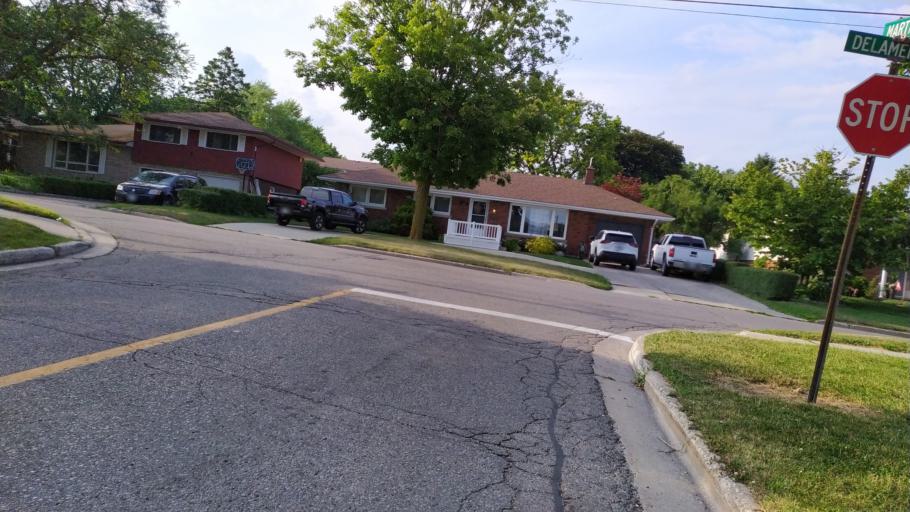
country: CA
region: Ontario
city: Stratford
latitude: 43.3786
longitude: -80.9650
